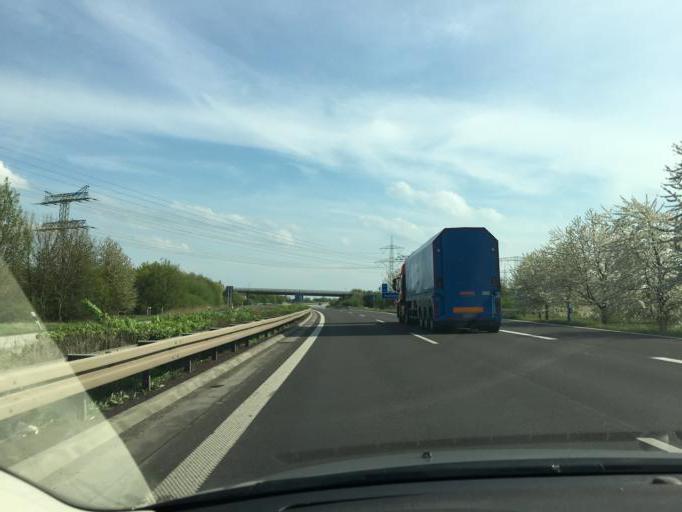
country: DE
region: Saxony-Anhalt
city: Dahlenwarsleben
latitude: 52.2035
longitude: 11.5468
